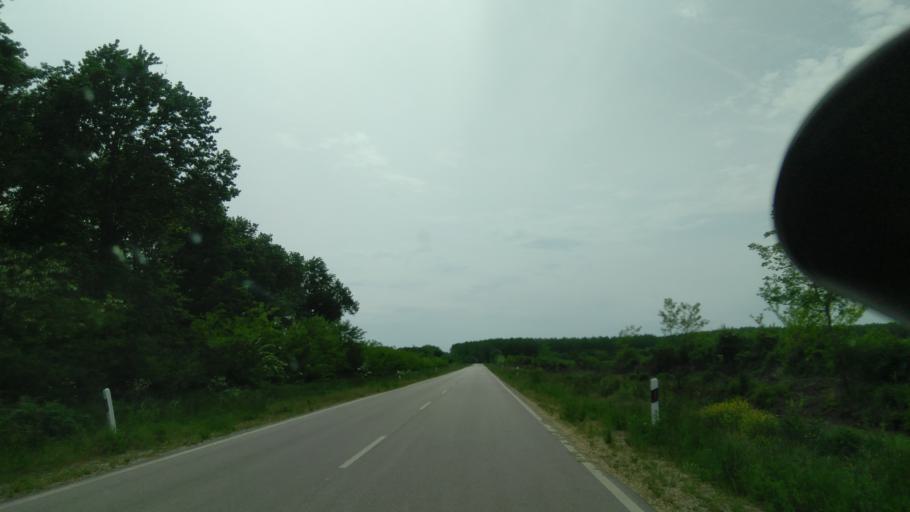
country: HU
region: Bekes
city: Mehkerek
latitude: 46.8618
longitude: 21.4494
